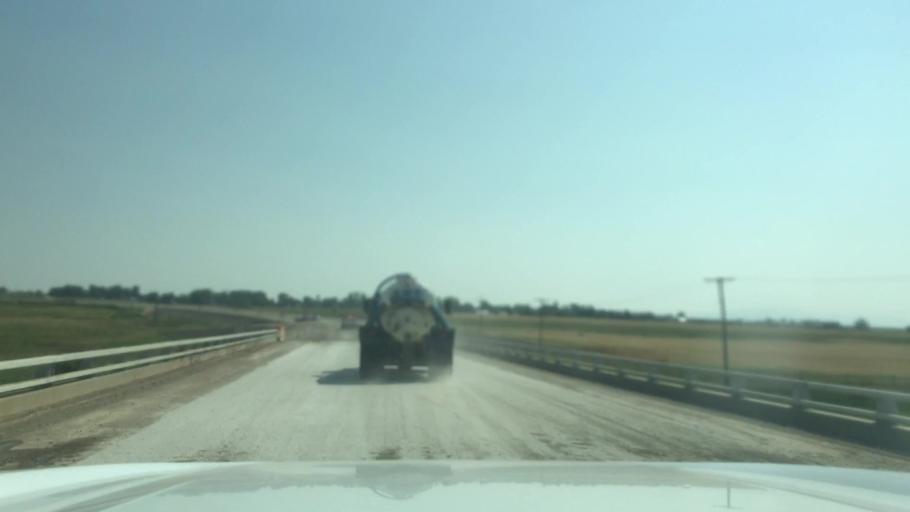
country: US
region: Montana
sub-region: Judith Basin County
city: Stanford
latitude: 47.0114
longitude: -109.8723
